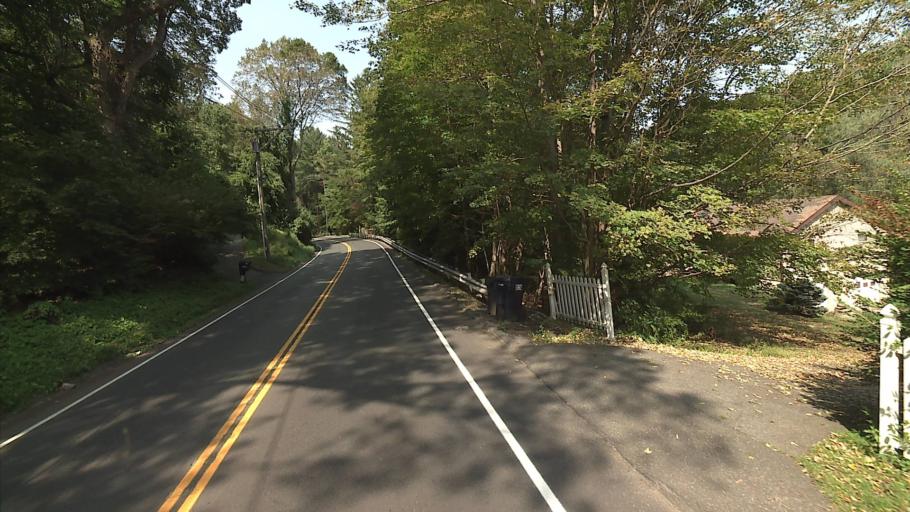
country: US
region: Connecticut
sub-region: Fairfield County
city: Bethel
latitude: 41.3713
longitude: -73.3911
